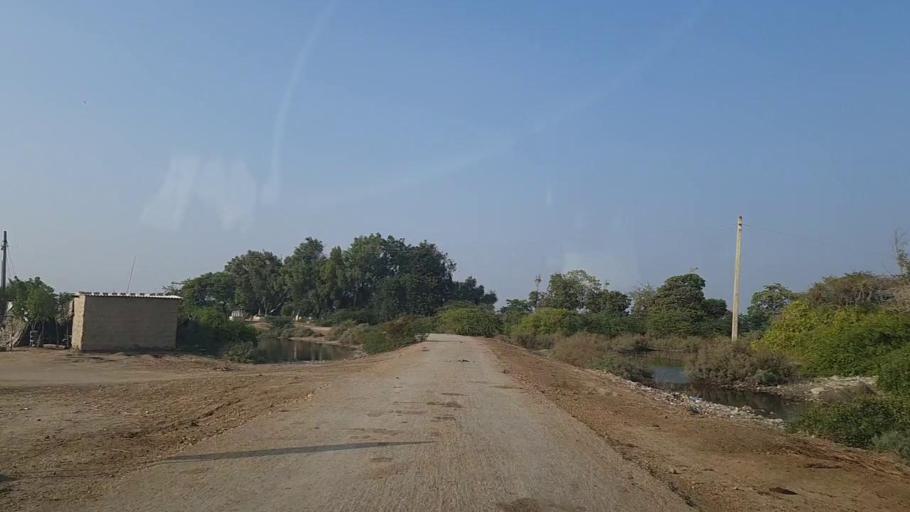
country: PK
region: Sindh
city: Mirpur Sakro
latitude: 24.5730
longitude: 67.6659
